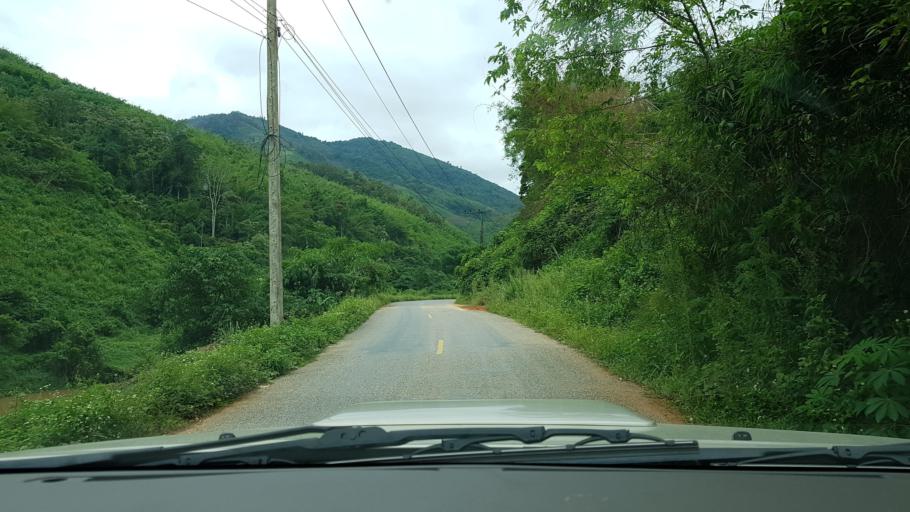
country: LA
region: Oudomxai
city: Muang La
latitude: 20.9273
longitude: 102.2053
